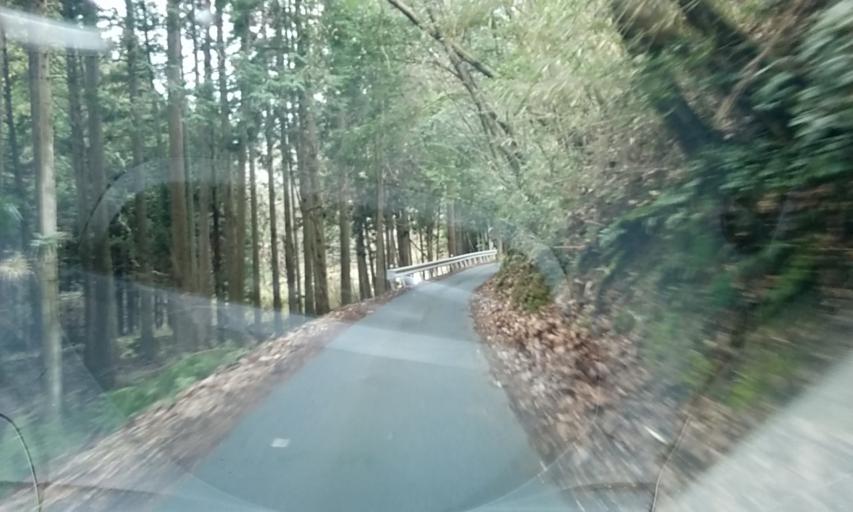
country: JP
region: Kyoto
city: Kameoka
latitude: 35.1117
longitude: 135.4344
